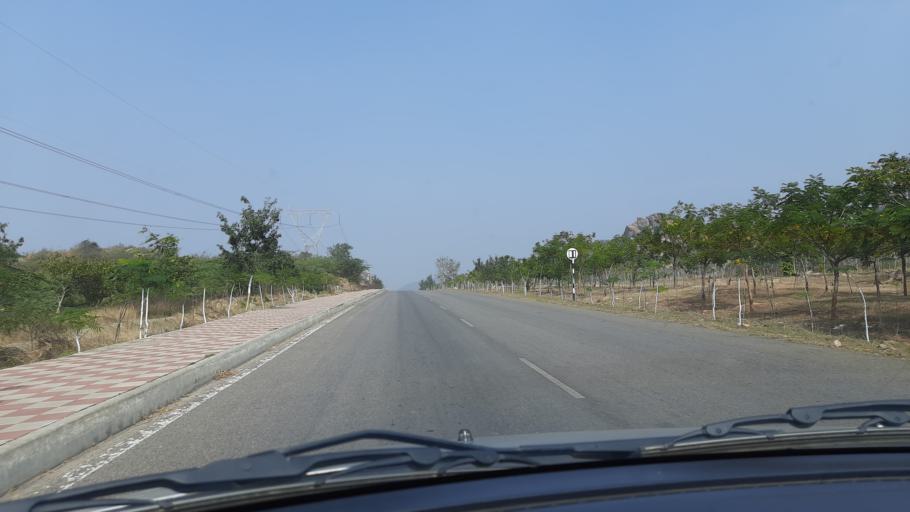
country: IN
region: Telangana
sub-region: Rangareddi
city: Lal Bahadur Nagar
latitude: 17.2941
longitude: 78.6521
